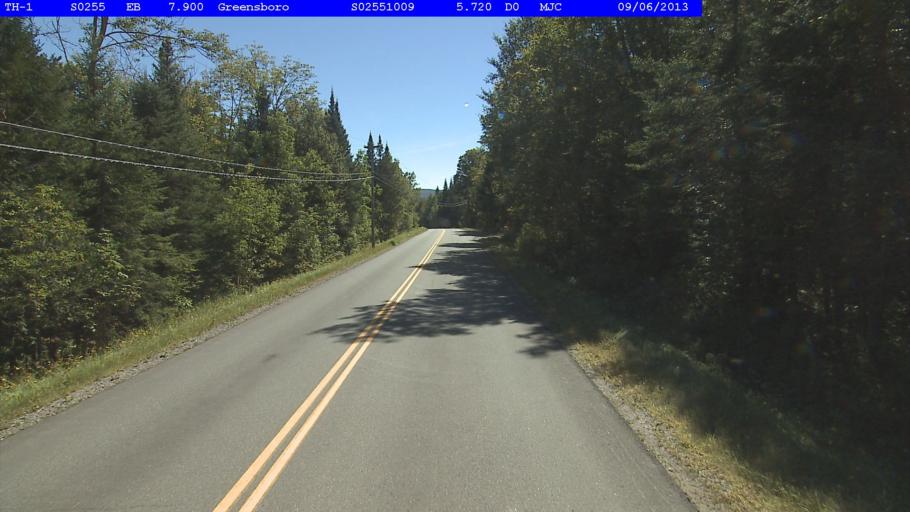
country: US
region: Vermont
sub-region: Caledonia County
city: Hardwick
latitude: 44.5687
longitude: -72.2886
